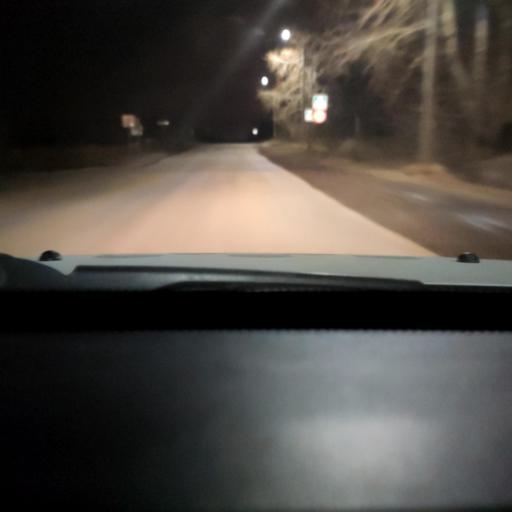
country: RU
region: Perm
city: Gamovo
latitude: 57.8745
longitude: 56.1020
